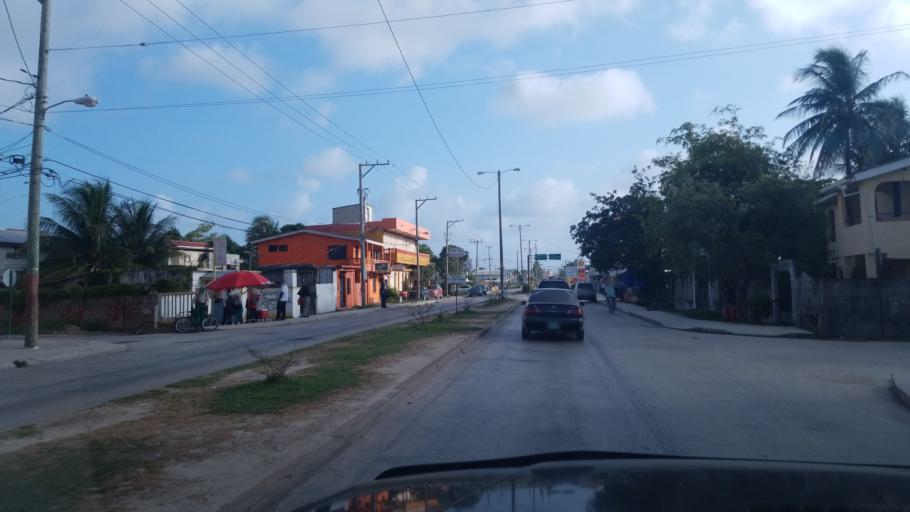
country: BZ
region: Belize
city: Belize City
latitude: 17.4934
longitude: -88.1991
